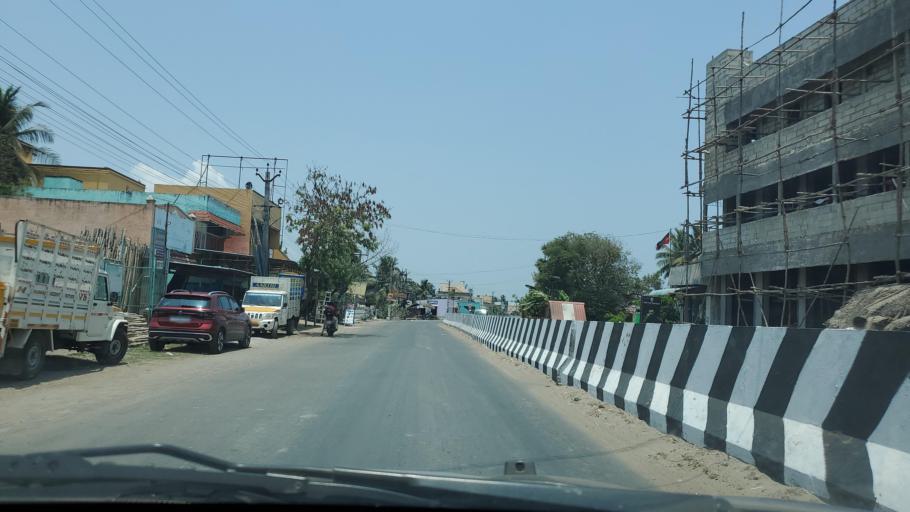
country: IN
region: Tamil Nadu
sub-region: Kancheepuram
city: Vengavasal
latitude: 12.8583
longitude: 80.1725
